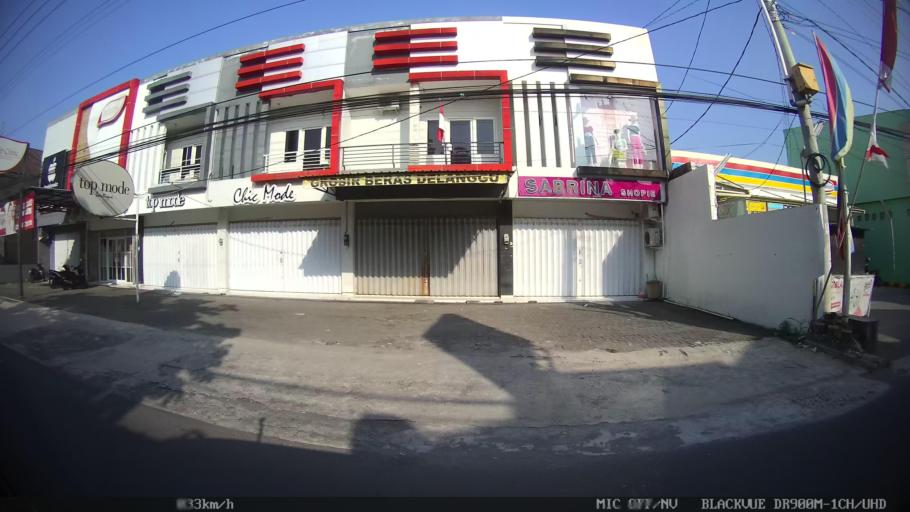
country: ID
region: Daerah Istimewa Yogyakarta
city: Depok
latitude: -7.7696
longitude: 110.4053
